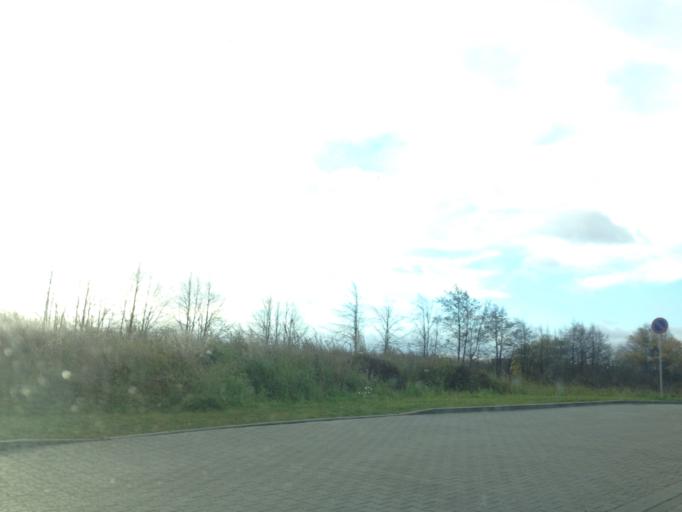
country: PL
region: Pomeranian Voivodeship
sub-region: Powiat gdanski
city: Kowale
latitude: 54.3089
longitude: 18.5620
